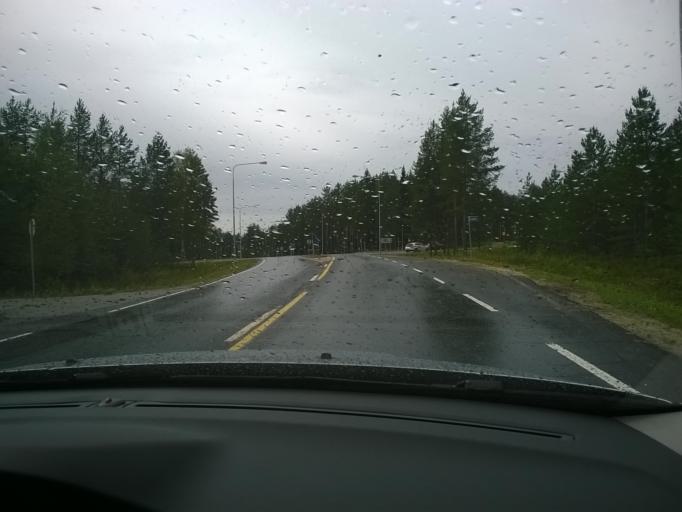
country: FI
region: Kainuu
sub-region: Kehys-Kainuu
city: Kuhmo
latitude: 64.1207
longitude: 29.5496
